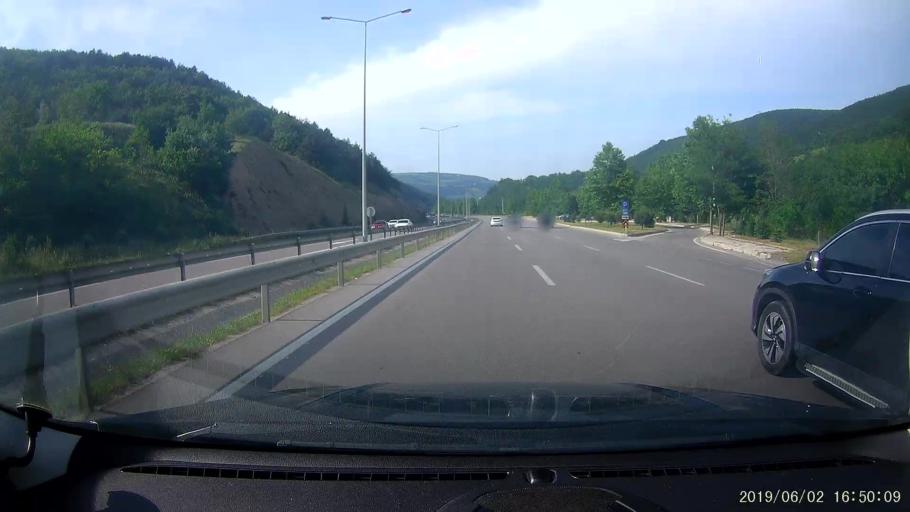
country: TR
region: Samsun
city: Samsun
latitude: 41.2488
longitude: 36.1732
